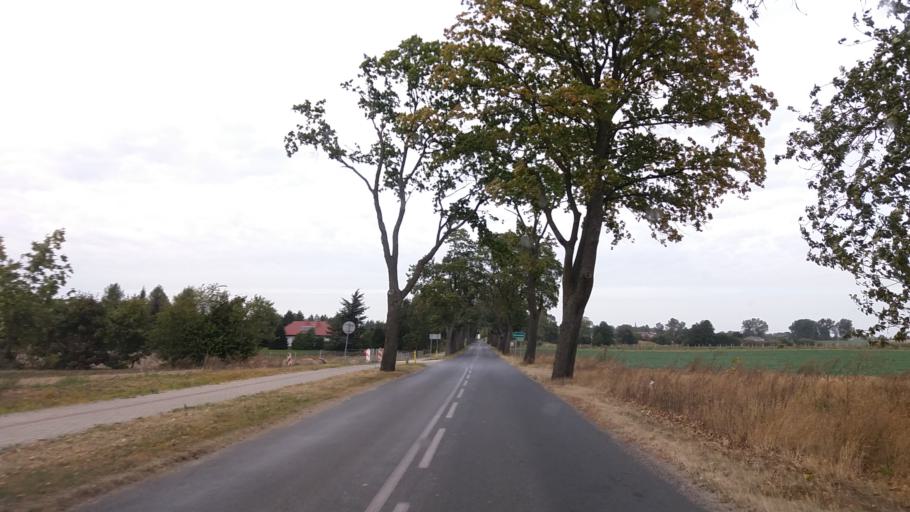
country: PL
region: Lubusz
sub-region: Powiat strzelecko-drezdenecki
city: Strzelce Krajenskie
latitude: 52.8951
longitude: 15.5097
